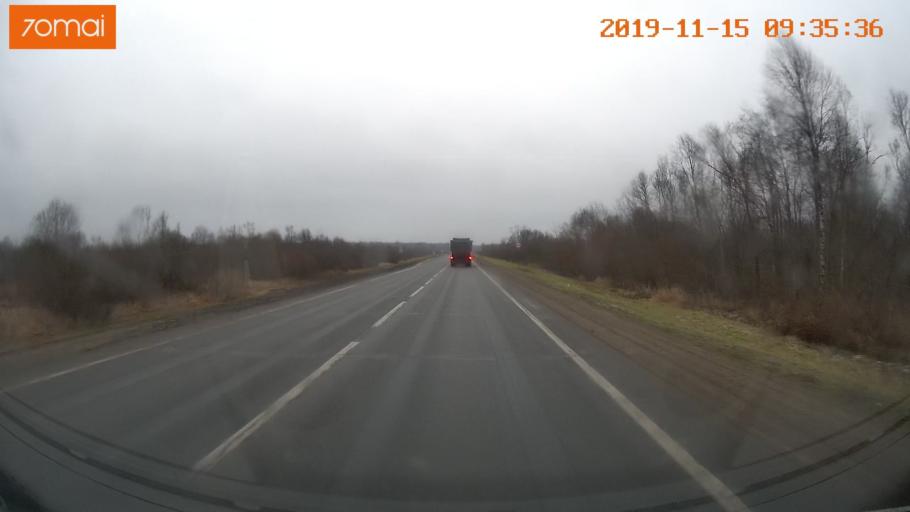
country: RU
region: Vologda
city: Sheksna
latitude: 59.2534
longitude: 38.4028
